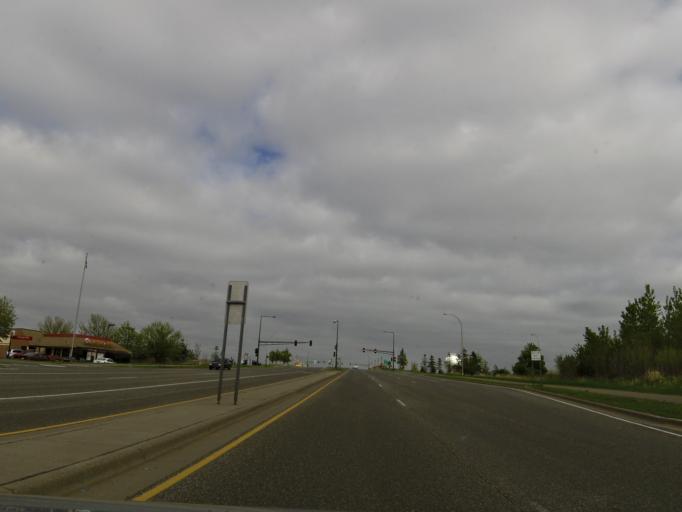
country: US
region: Minnesota
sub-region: Washington County
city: Woodbury
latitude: 44.9263
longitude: -92.9723
